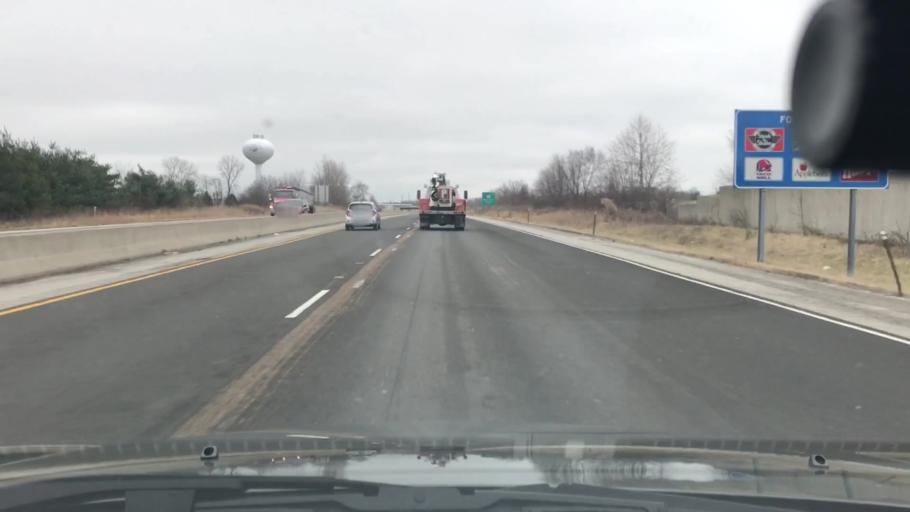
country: US
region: Illinois
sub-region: Madison County
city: Rosewood Heights
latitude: 38.8935
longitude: -90.0634
